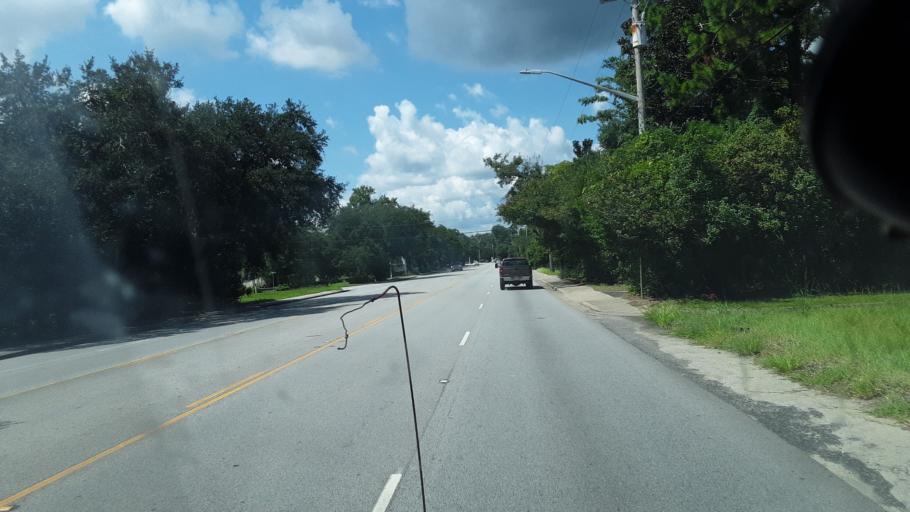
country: US
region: South Carolina
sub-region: Berkeley County
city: Moncks Corner
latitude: 33.1982
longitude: -80.0077
